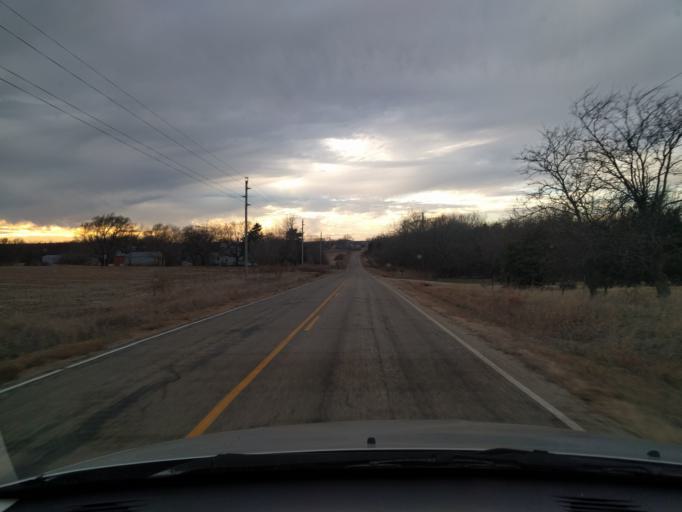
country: US
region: Kansas
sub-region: Clay County
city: Clay Center
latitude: 39.2487
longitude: -97.3262
